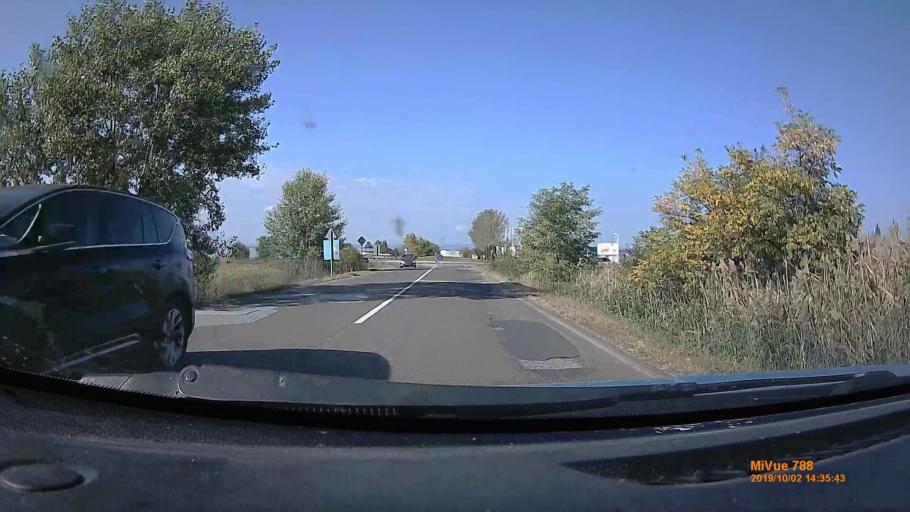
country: HU
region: Borsod-Abauj-Zemplen
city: Mezokovesd
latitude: 47.7870
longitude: 20.5789
